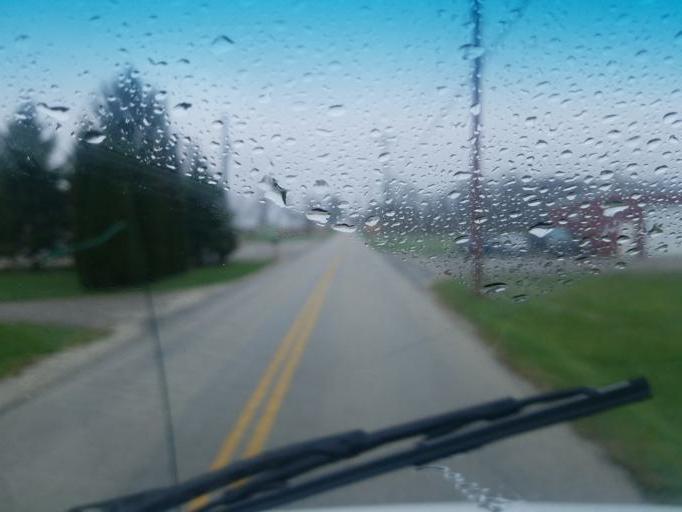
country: US
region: Ohio
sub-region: Wood County
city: North Baltimore
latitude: 41.1467
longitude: -83.6312
